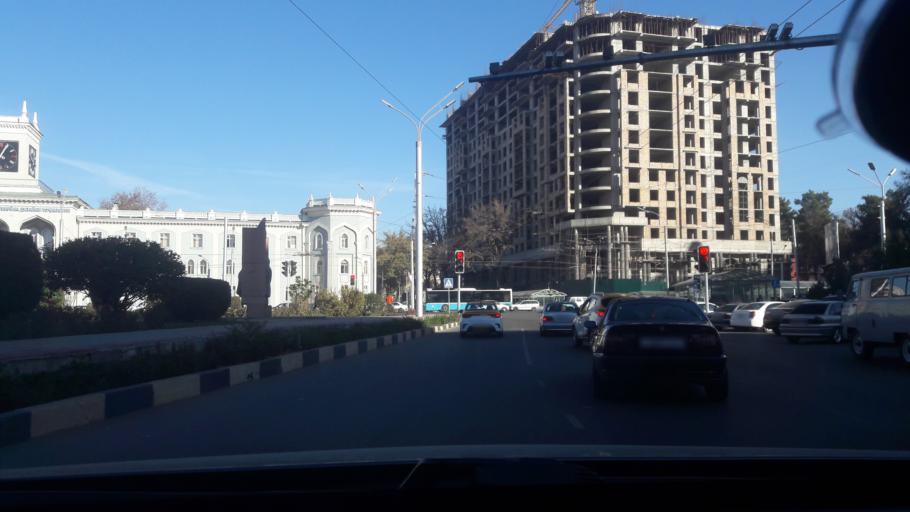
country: TJ
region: Dushanbe
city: Dushanbe
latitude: 38.5622
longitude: 68.7994
